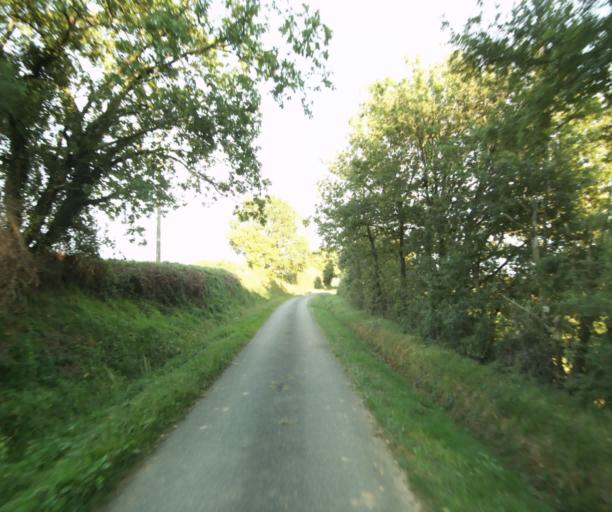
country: FR
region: Midi-Pyrenees
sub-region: Departement du Gers
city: Eauze
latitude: 43.8792
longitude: 0.0123
